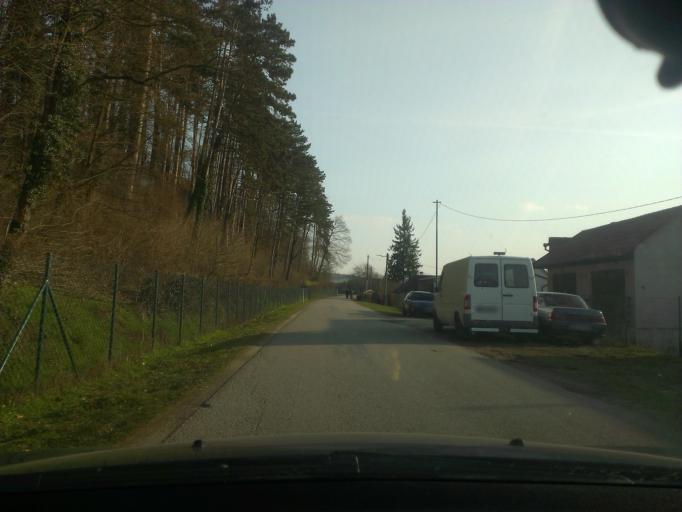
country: SK
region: Trnavsky
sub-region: Okres Trnava
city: Piestany
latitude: 48.6610
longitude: 17.8794
